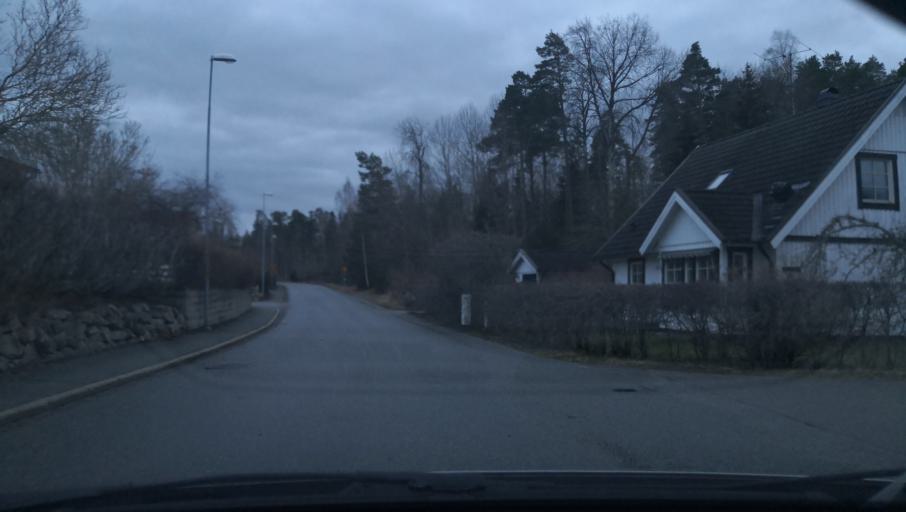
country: SE
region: Stockholm
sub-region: Taby Kommun
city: Taby
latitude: 59.4674
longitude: 18.0342
